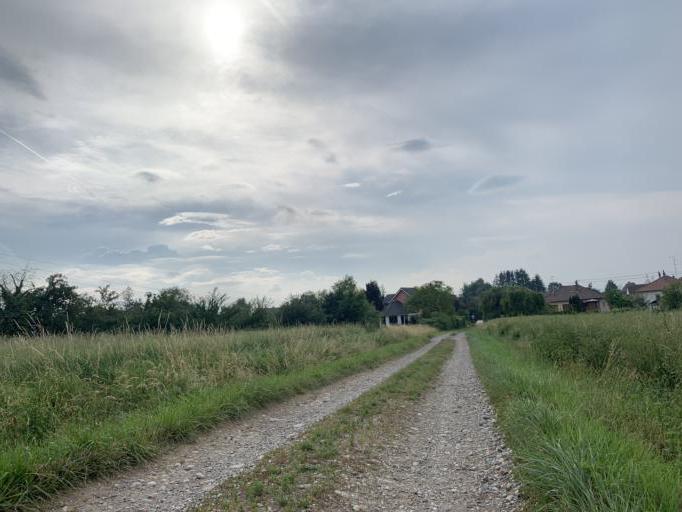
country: FR
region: Alsace
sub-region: Departement du Haut-Rhin
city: Morschwiller-le-Bas
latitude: 47.7327
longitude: 7.2653
